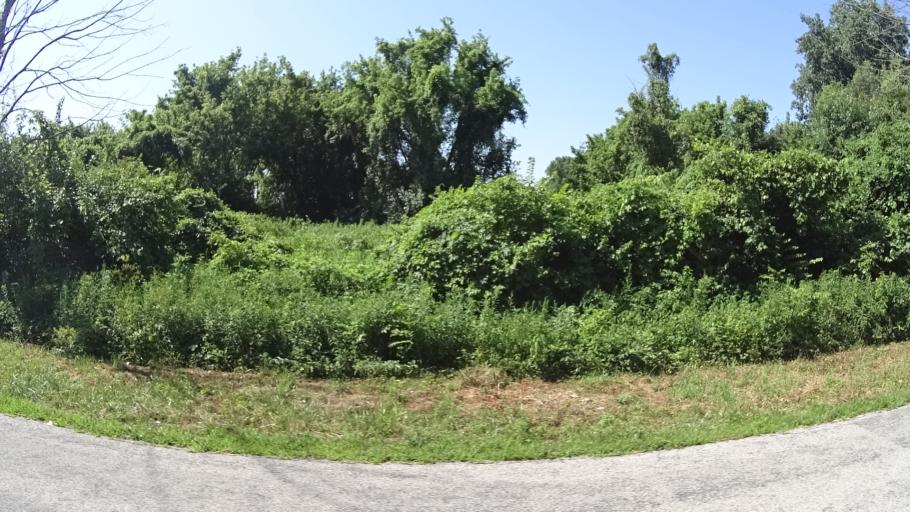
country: US
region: Ohio
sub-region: Erie County
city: Sandusky
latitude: 41.4082
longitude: -82.8283
